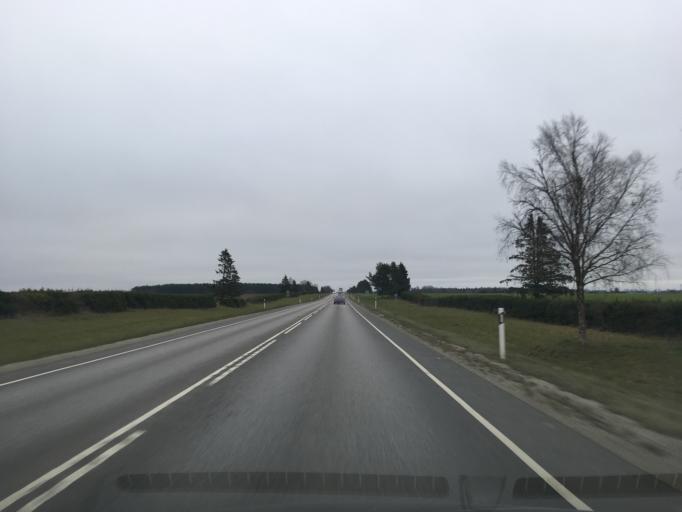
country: EE
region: Laeaene-Virumaa
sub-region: Haljala vald
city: Haljala
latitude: 59.4199
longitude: 26.3061
